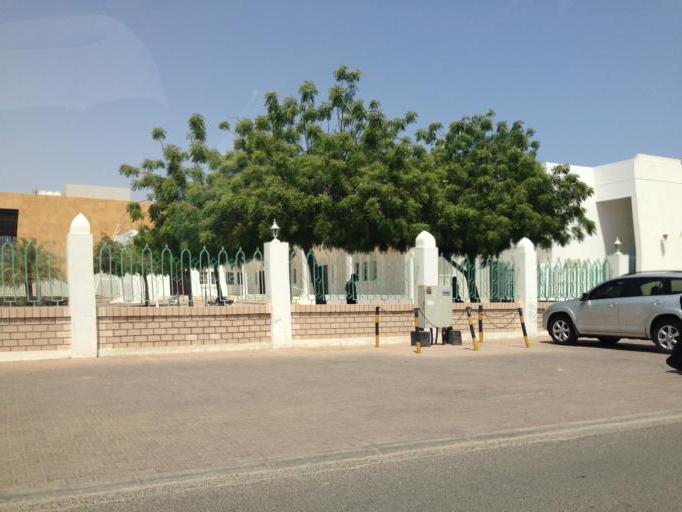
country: OM
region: Muhafazat Masqat
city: Bawshar
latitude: 23.6034
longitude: 58.3648
